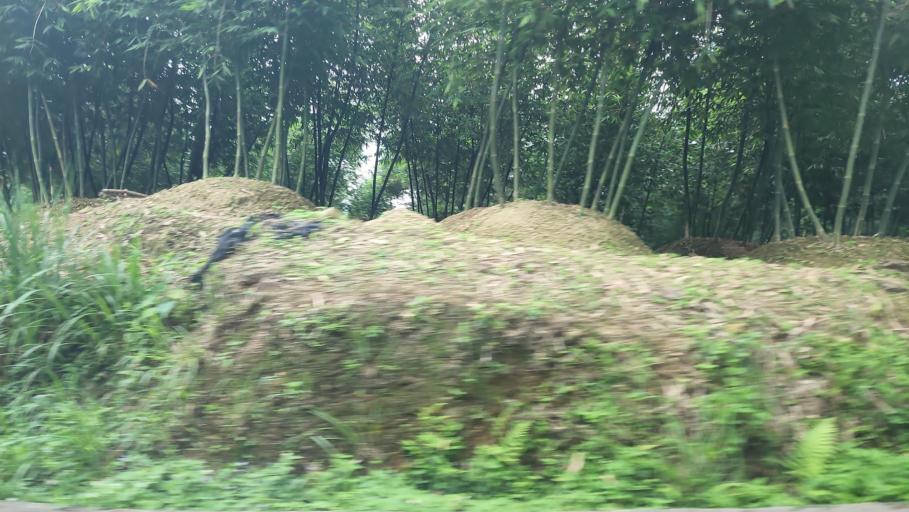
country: TW
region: Taiwan
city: Daxi
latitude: 24.8840
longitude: 121.4185
